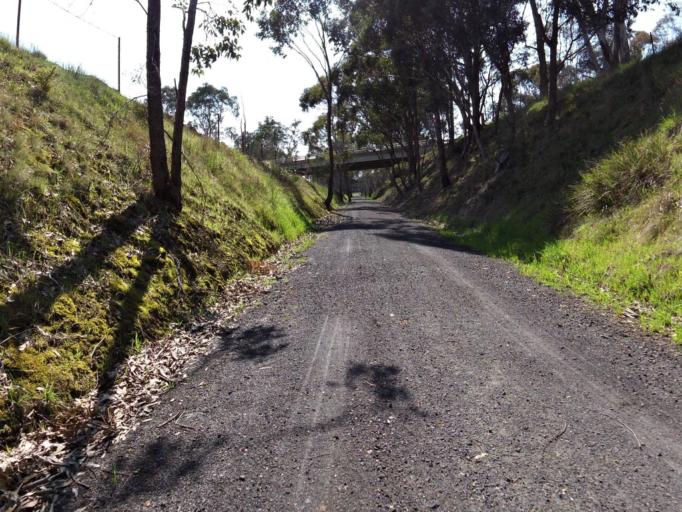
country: AU
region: Victoria
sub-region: Murrindindi
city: Alexandra
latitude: -37.1169
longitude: 145.6054
